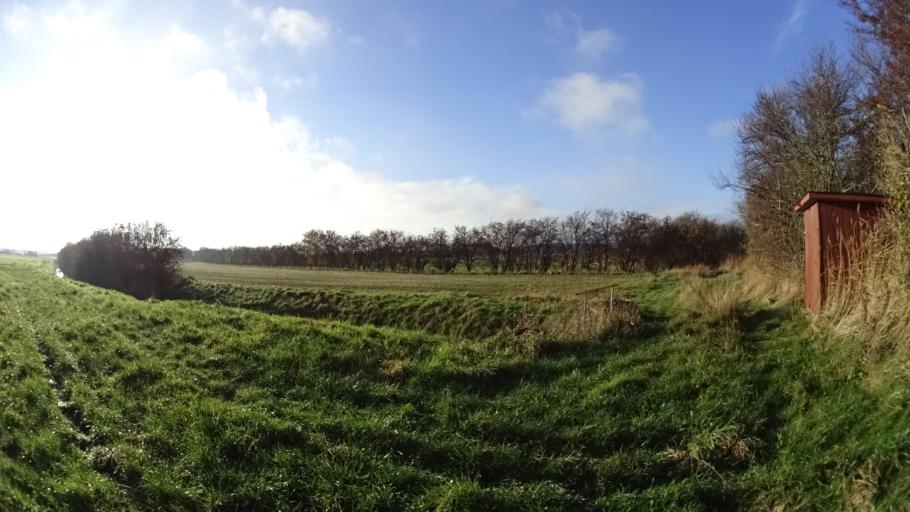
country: DK
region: Central Jutland
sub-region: Arhus Kommune
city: Beder
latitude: 56.0187
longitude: 10.2577
